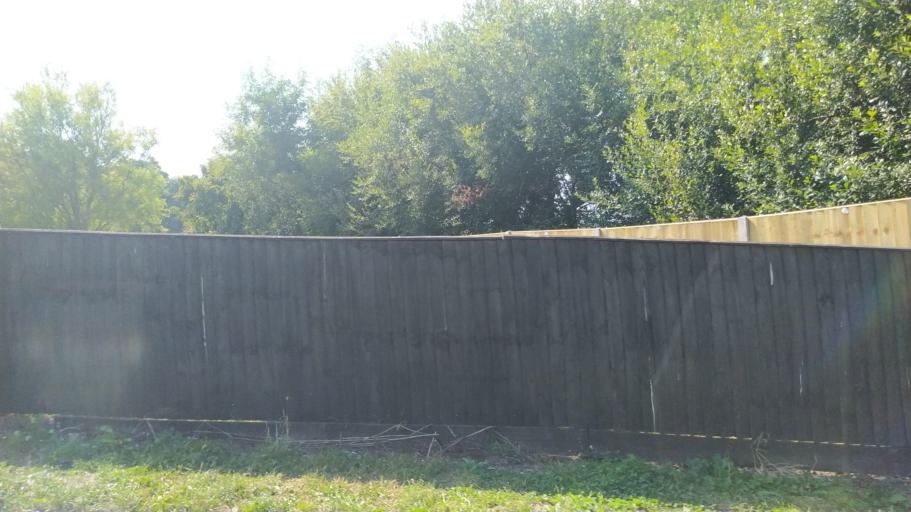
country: GB
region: England
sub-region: Hampshire
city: Cadnam
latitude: 50.9073
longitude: -1.5386
